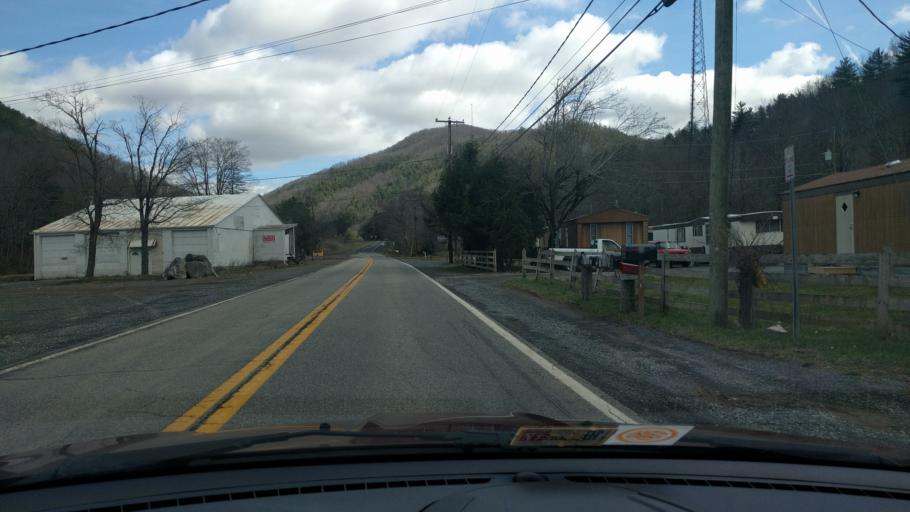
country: US
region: West Virginia
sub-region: Greenbrier County
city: White Sulphur Springs
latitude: 37.7935
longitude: -80.2742
